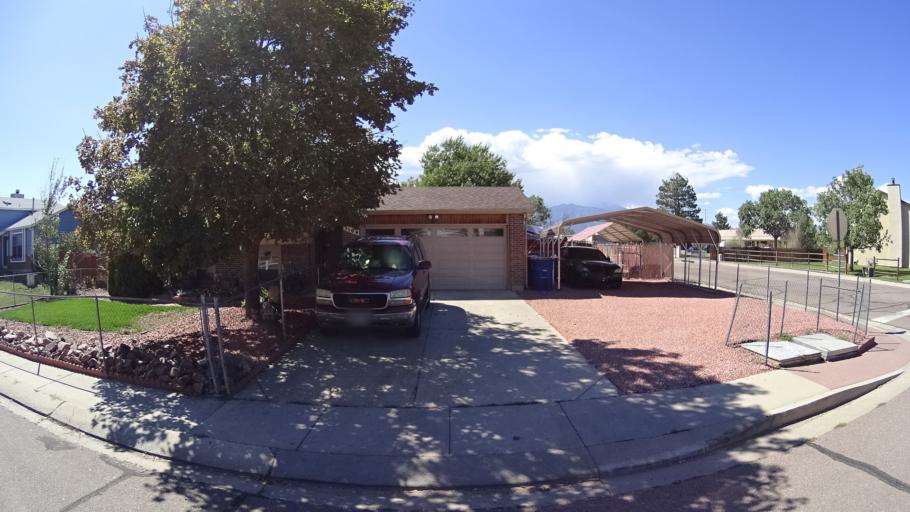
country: US
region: Colorado
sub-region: El Paso County
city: Stratmoor
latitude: 38.7873
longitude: -104.7524
